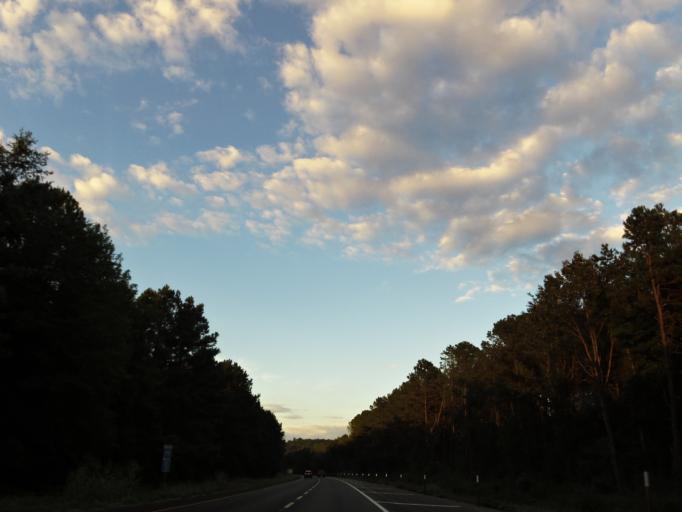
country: US
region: Tennessee
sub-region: Bradley County
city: Hopewell
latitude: 35.3288
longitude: -84.7619
